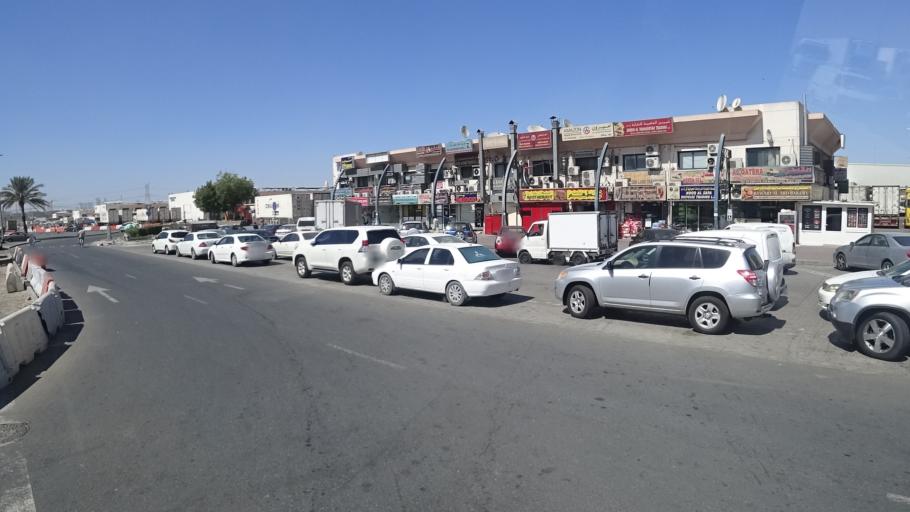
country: AE
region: Ash Shariqah
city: Sharjah
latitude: 25.1748
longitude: 55.3941
